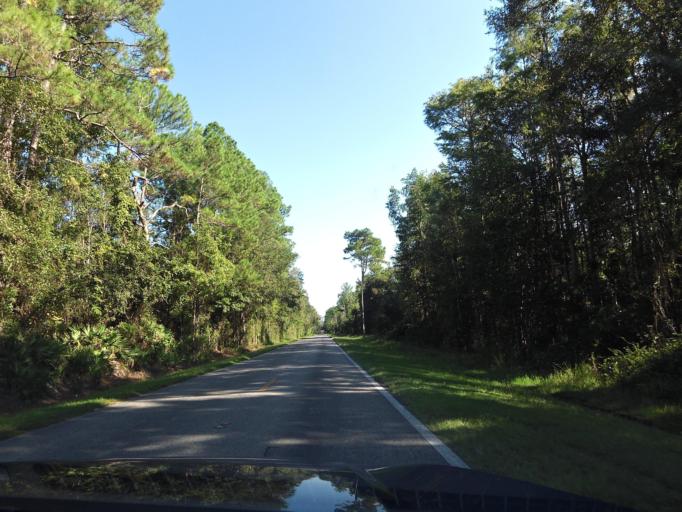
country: US
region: Florida
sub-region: Putnam County
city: East Palatka
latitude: 29.7827
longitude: -81.4916
